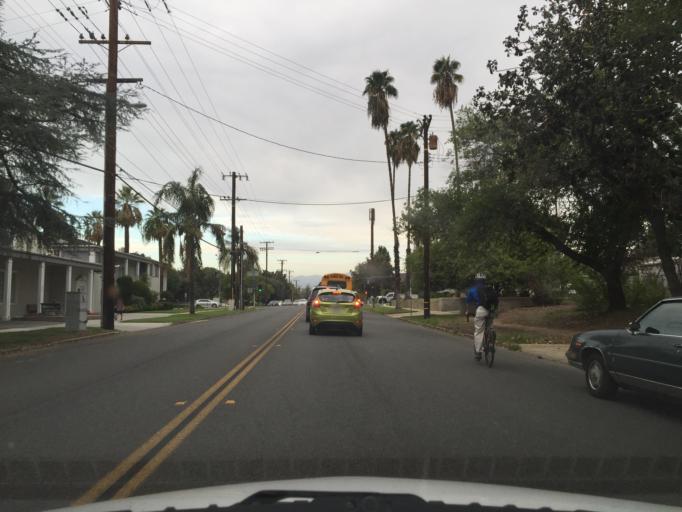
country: US
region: California
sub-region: San Bernardino County
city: Redlands
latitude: 34.0517
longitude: -117.1903
